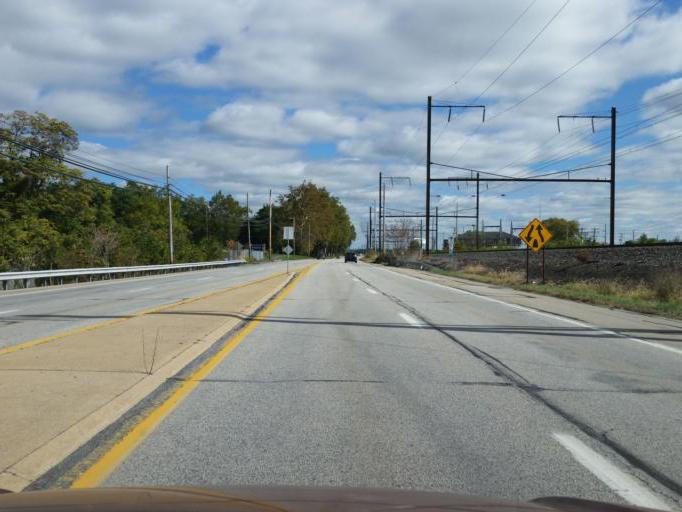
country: US
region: Pennsylvania
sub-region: Dauphin County
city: Middletown
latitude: 40.1983
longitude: -76.7527
